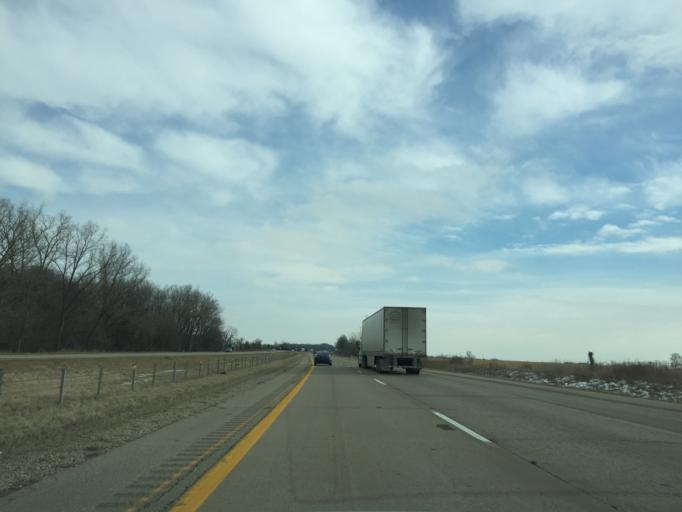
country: US
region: Michigan
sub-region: Ionia County
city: Saranac
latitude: 42.8788
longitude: -85.1509
